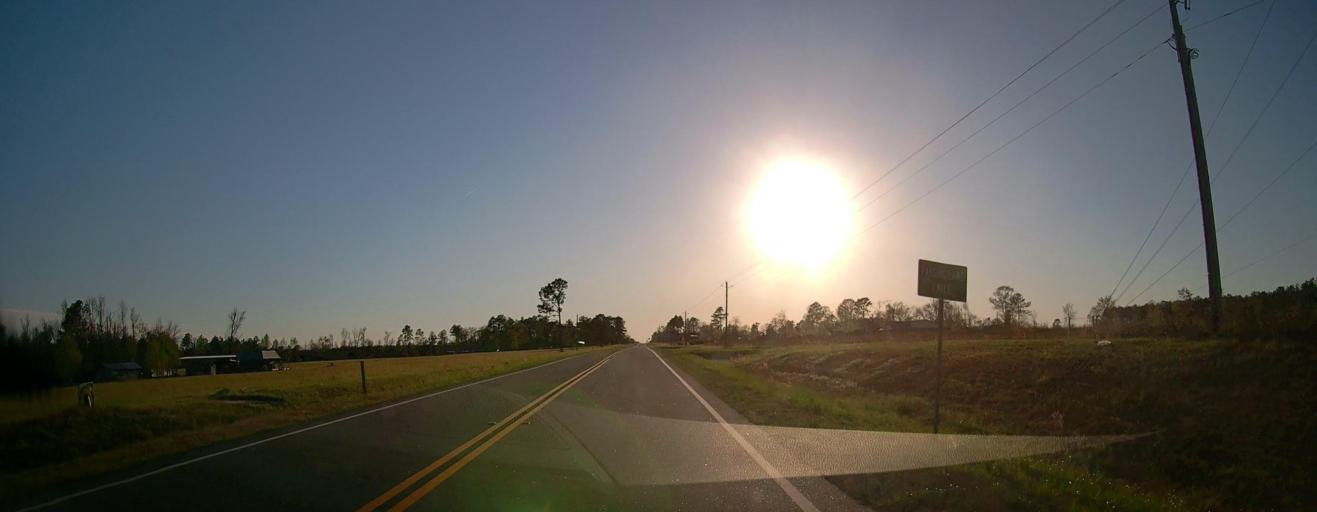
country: US
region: Georgia
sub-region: Wilcox County
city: Abbeville
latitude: 31.9713
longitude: -83.3715
